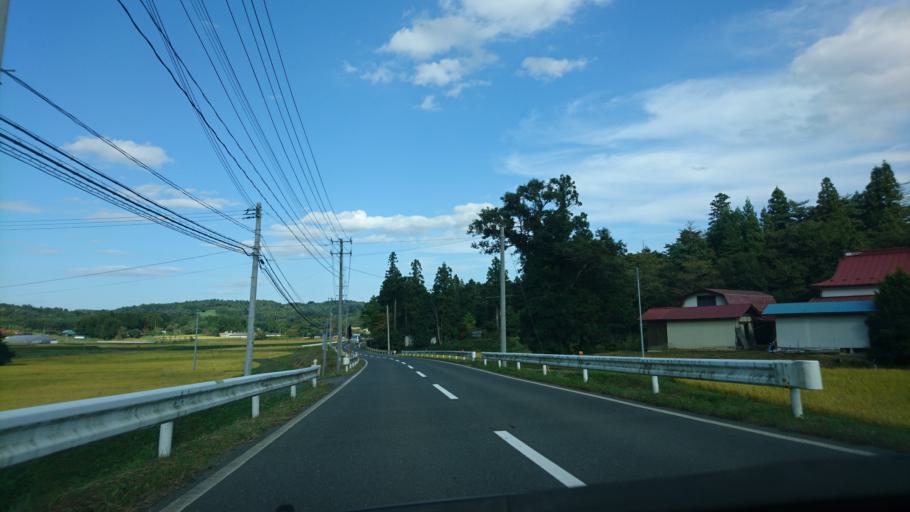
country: JP
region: Iwate
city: Ichinoseki
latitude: 38.8333
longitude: 141.2278
